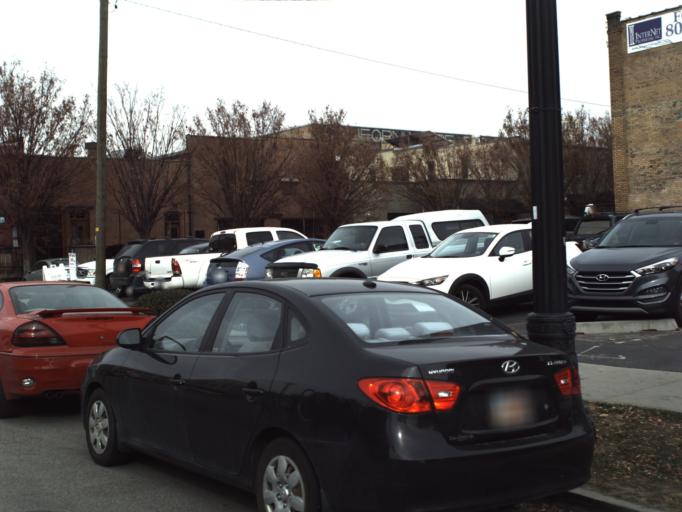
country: US
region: Utah
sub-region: Salt Lake County
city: Salt Lake City
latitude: 40.7635
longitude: -111.9024
